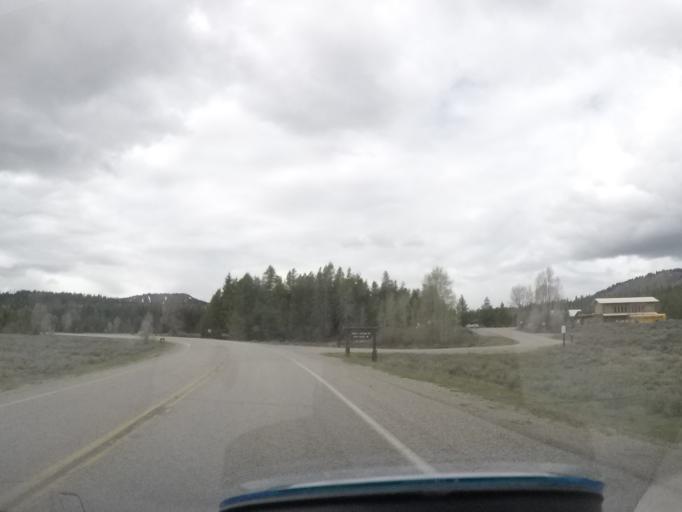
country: US
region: Wyoming
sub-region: Teton County
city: Jackson
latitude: 43.8399
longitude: -110.5057
